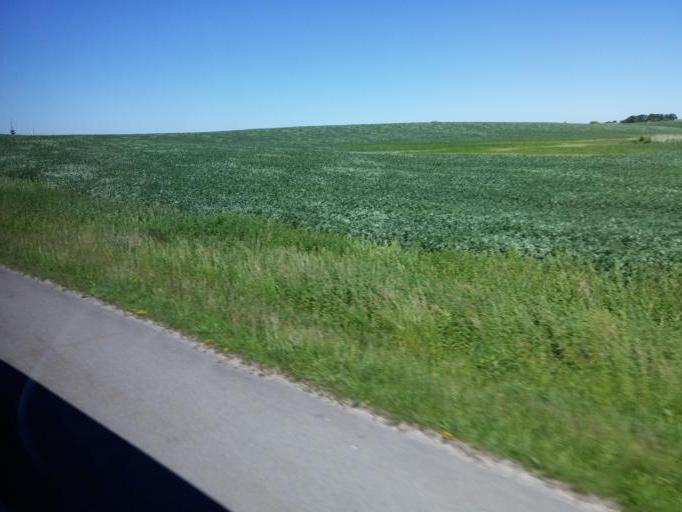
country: SE
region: Skane
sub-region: Malmo
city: Oxie
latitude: 55.5571
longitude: 13.0919
